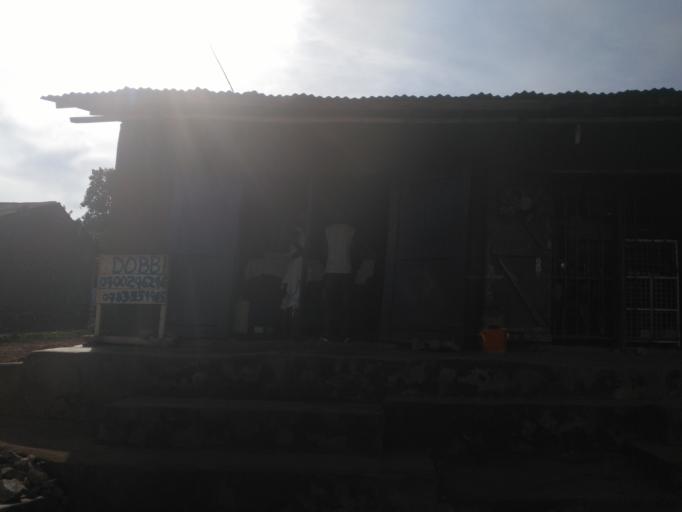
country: UG
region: Central Region
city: Kampala Central Division
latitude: 0.3615
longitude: 32.5698
